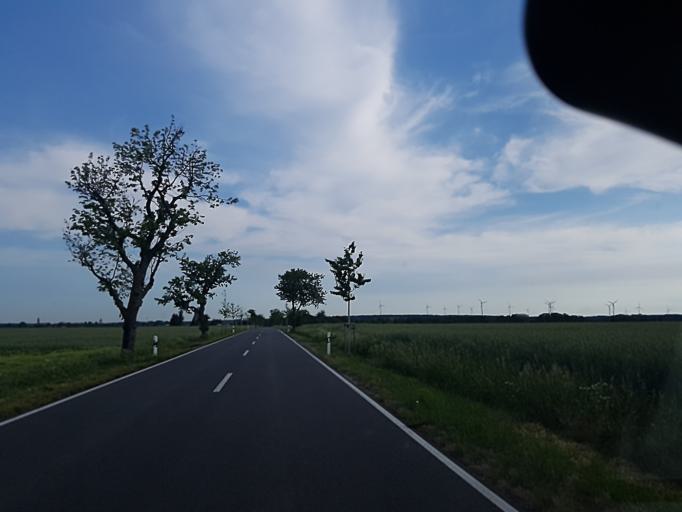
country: DE
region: Brandenburg
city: Niemegk
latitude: 52.0539
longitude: 12.6936
